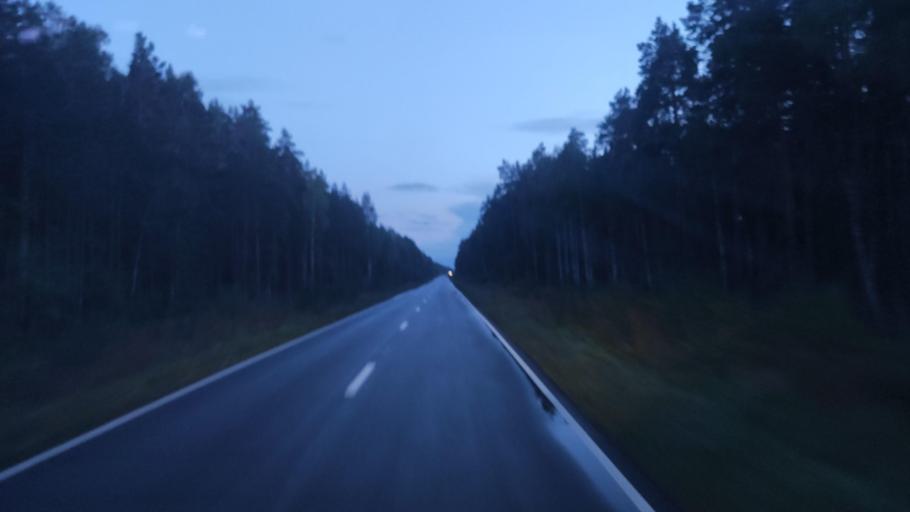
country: RU
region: Vladimir
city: Galitsy
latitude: 56.0668
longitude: 42.8665
